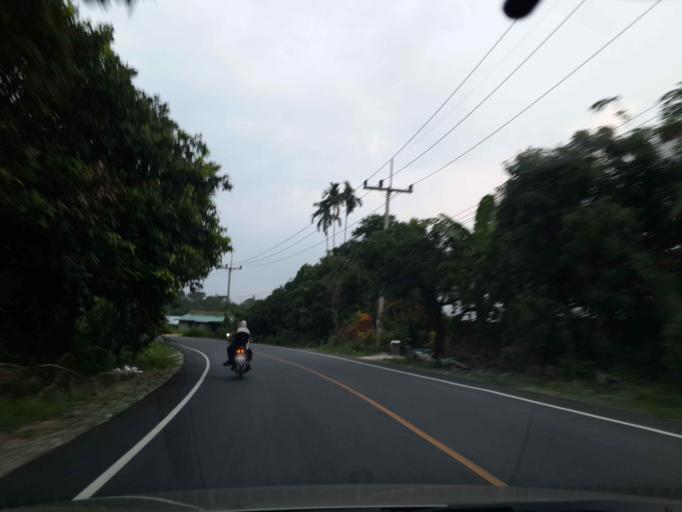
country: TH
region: Narathiwat
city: Rueso
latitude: 6.3450
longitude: 101.4802
